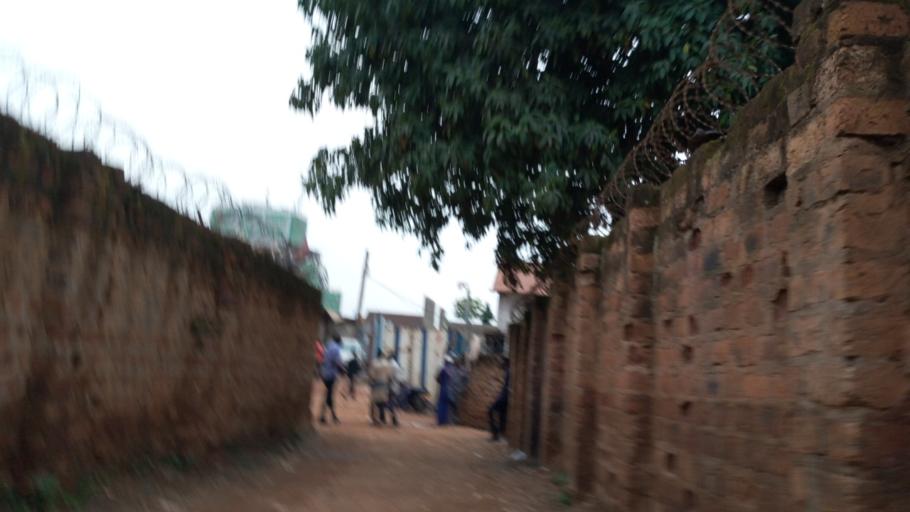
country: UG
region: Central Region
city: Kampala Central Division
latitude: 0.3274
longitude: 32.5688
